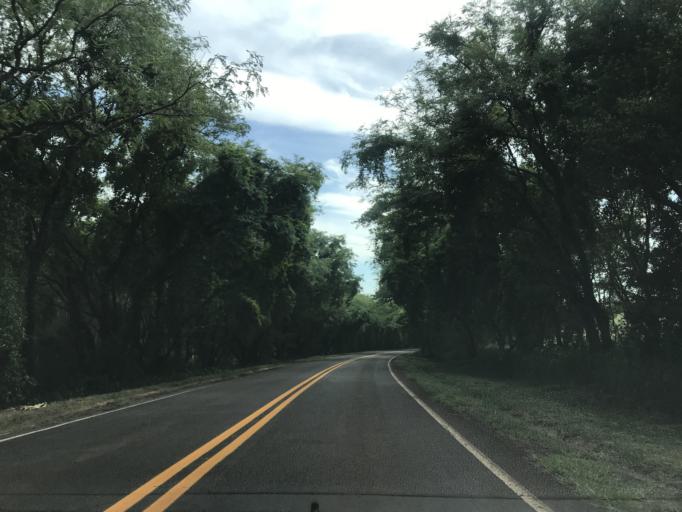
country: BR
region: Parana
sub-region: Terra Rica
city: Terra Rica
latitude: -22.7768
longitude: -52.6554
